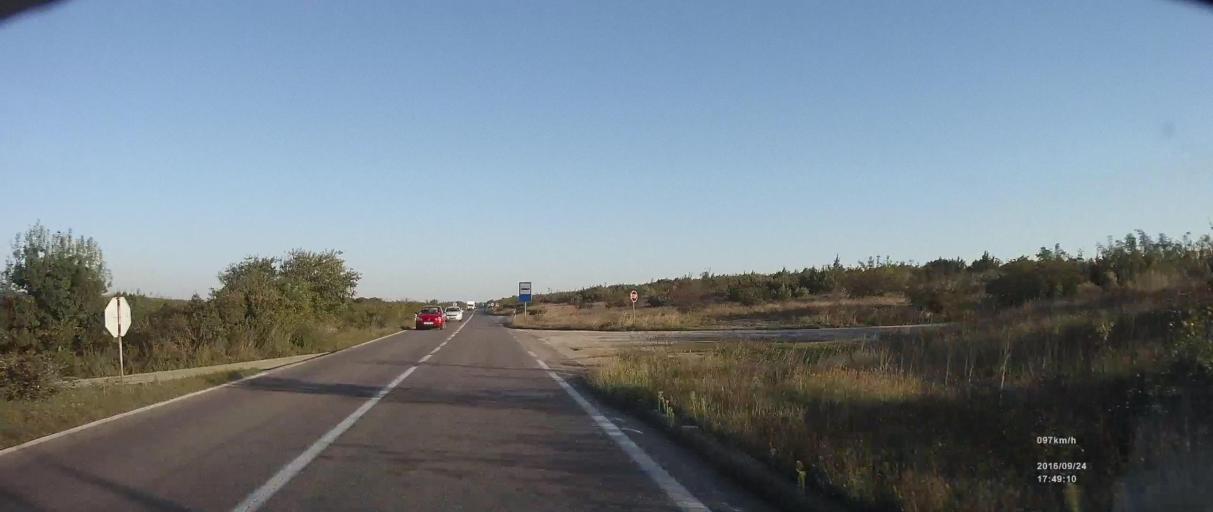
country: HR
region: Zadarska
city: Polaca
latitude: 44.0568
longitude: 15.5464
